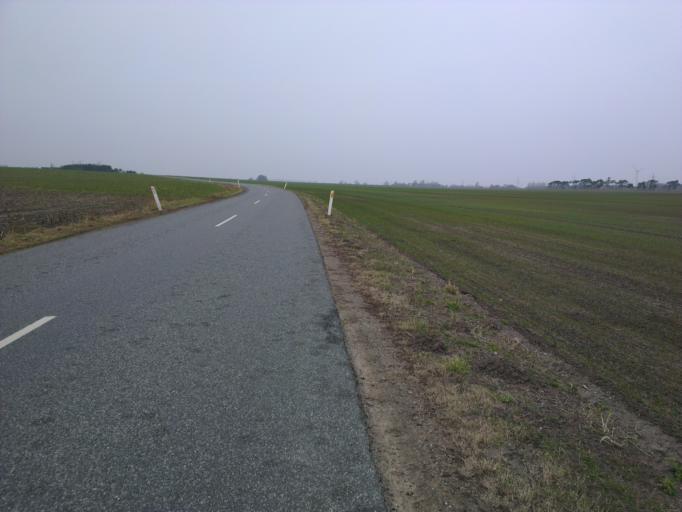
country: DK
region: Capital Region
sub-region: Frederikssund Kommune
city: Skibby
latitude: 55.7884
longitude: 11.9964
